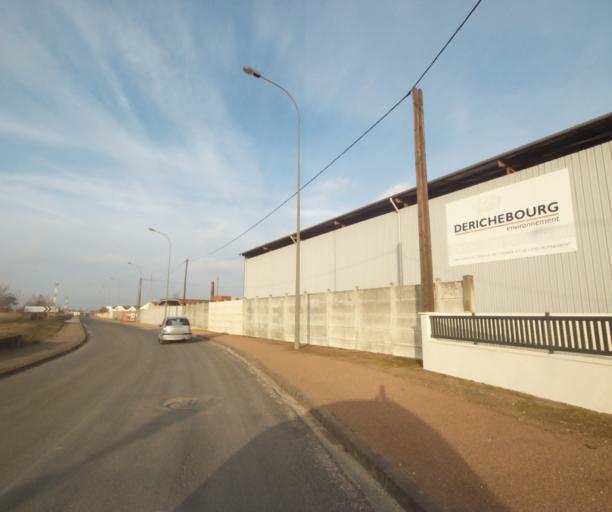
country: FR
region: Champagne-Ardenne
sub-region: Departement de la Haute-Marne
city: Saint-Dizier
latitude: 48.6453
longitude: 4.9445
